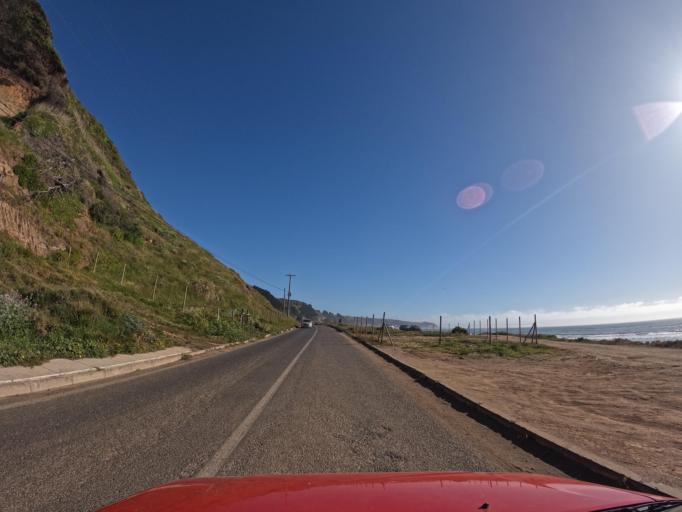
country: CL
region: Maule
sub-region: Provincia de Talca
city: Constitucion
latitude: -34.8618
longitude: -72.1473
